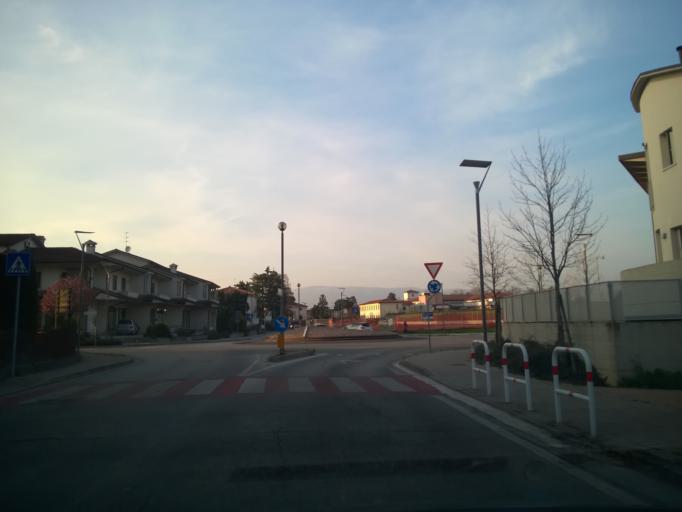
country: IT
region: Veneto
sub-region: Provincia di Vicenza
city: Caldogno-Rettorgole-Cresole
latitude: 45.6116
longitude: 11.5076
